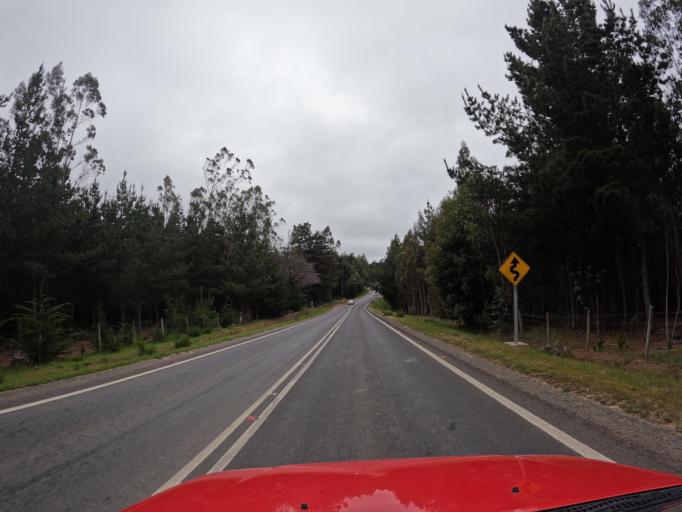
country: CL
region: O'Higgins
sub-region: Provincia de Colchagua
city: Santa Cruz
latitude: -34.5920
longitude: -72.0157
